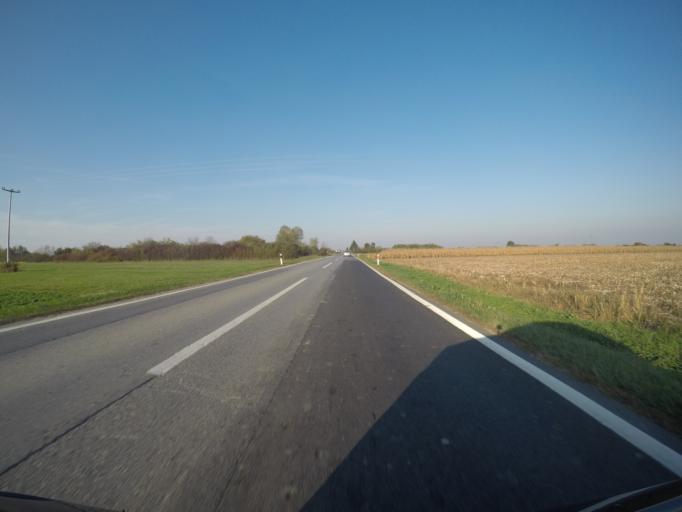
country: HU
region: Somogy
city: Barcs
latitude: 45.9199
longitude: 17.4511
